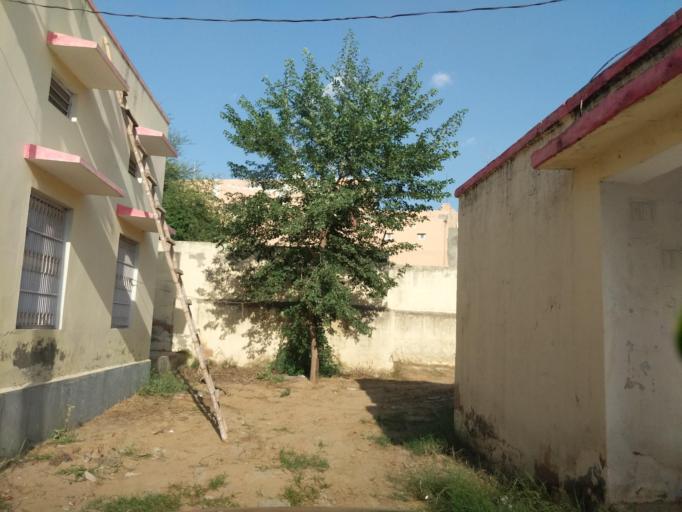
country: IN
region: Rajasthan
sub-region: Churu
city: Rajgarh
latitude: 28.5337
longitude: 75.3778
